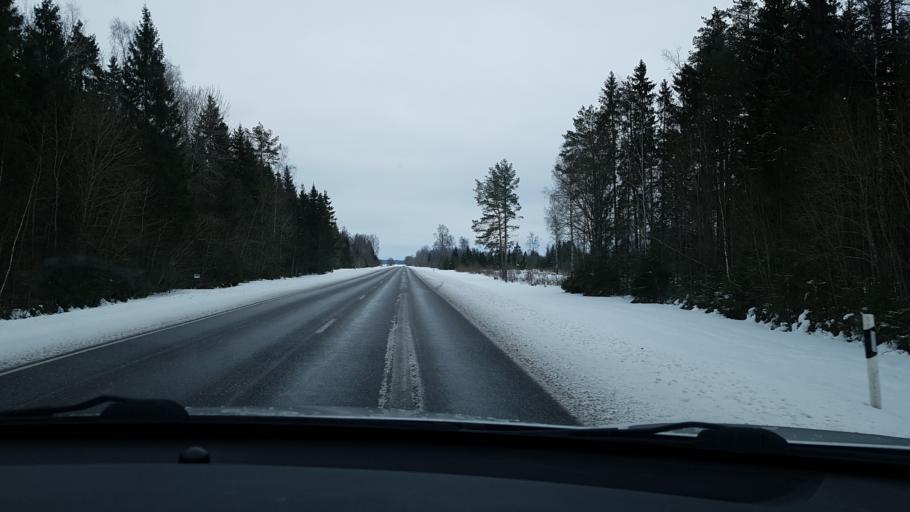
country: EE
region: Jaervamaa
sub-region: Jaerva-Jaani vald
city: Jarva-Jaani
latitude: 59.1317
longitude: 25.7780
